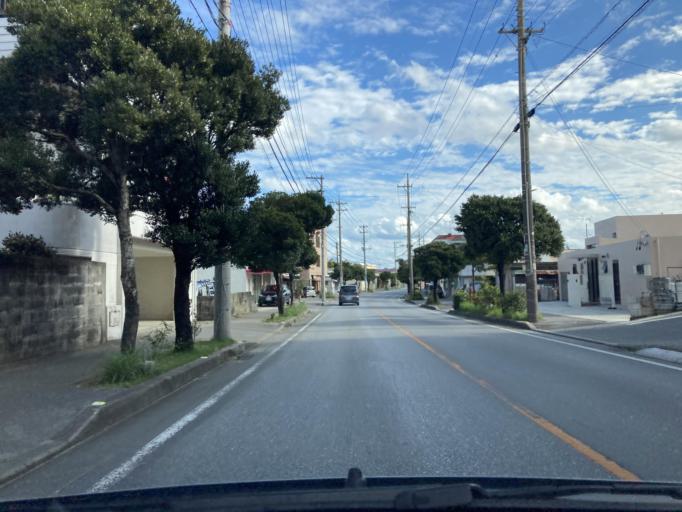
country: JP
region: Okinawa
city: Ishikawa
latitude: 26.4155
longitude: 127.8219
